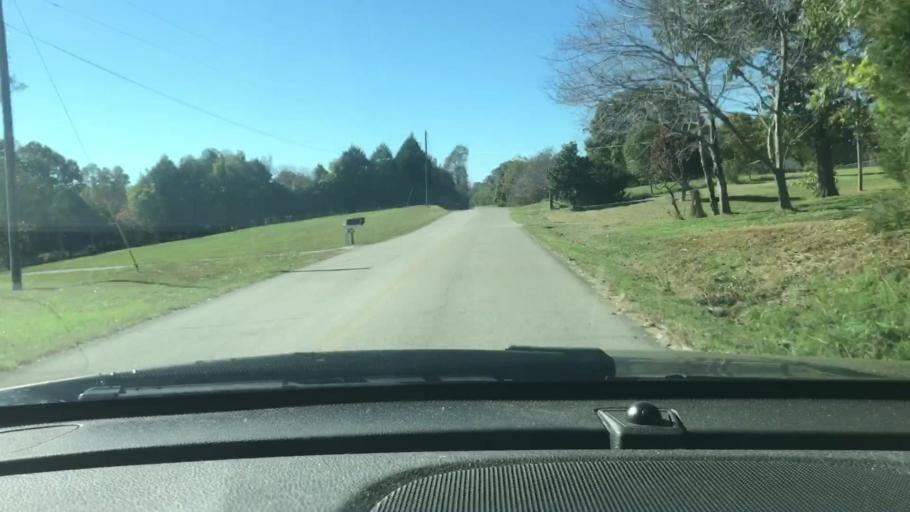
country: US
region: Tennessee
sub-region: Dickson County
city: Charlotte
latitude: 36.1805
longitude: -87.2964
